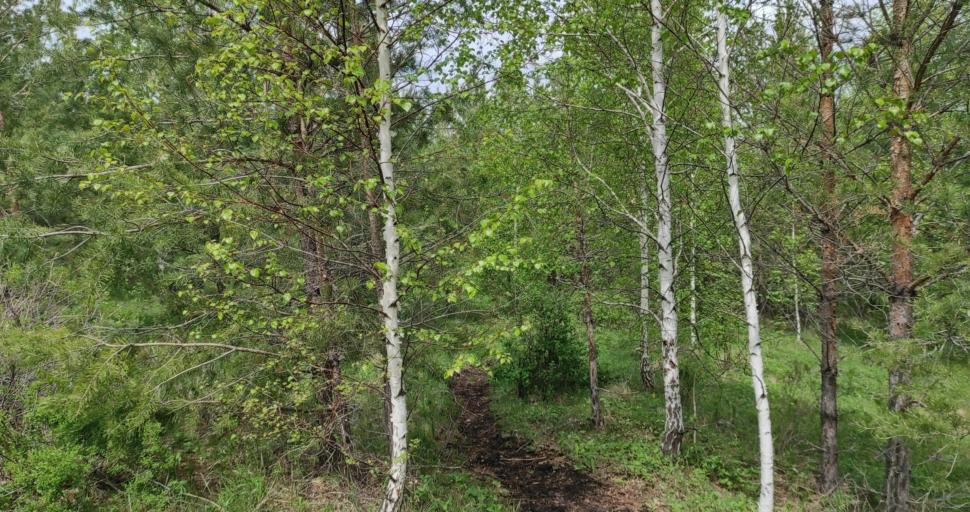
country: RU
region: Bashkortostan
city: Sibay
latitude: 52.6887
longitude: 58.5399
